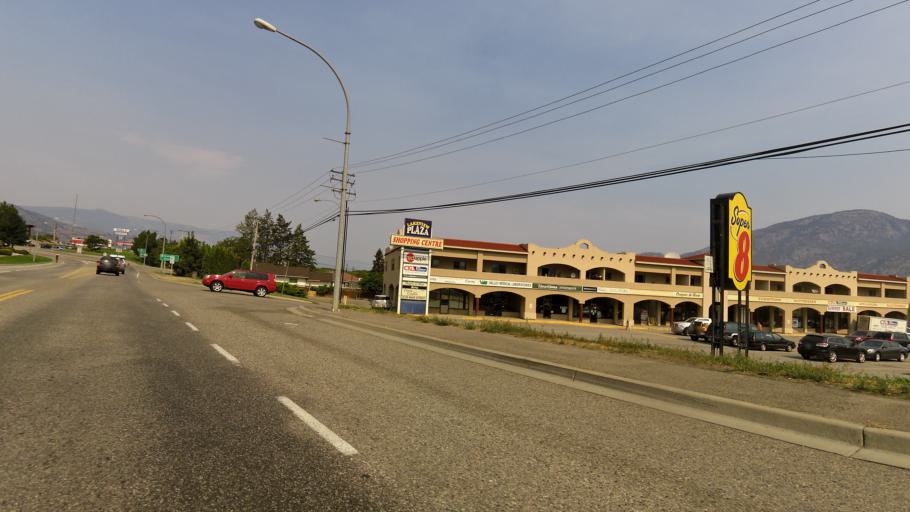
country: CA
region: British Columbia
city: Osoyoos
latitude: 49.0350
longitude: -119.4741
